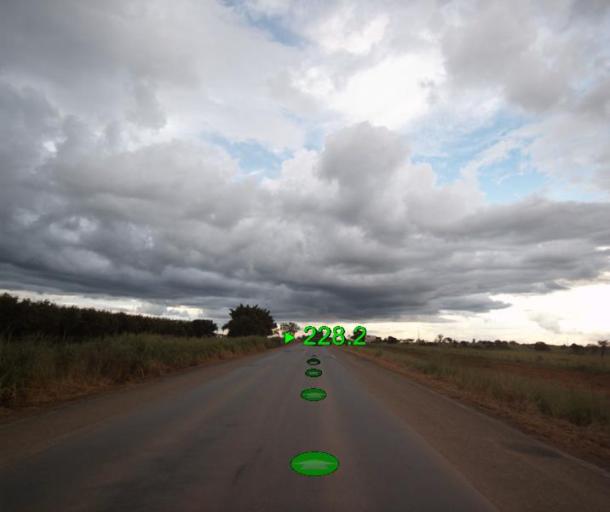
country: BR
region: Goias
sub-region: Uruacu
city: Uruacu
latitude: -14.7531
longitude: -49.2548
